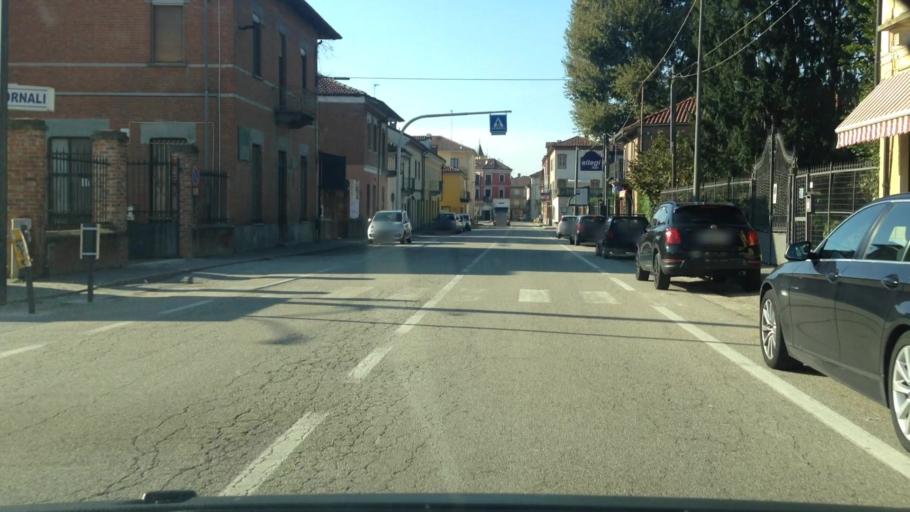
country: IT
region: Piedmont
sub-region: Provincia di Asti
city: Castello di Annone
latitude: 44.8784
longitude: 8.3161
